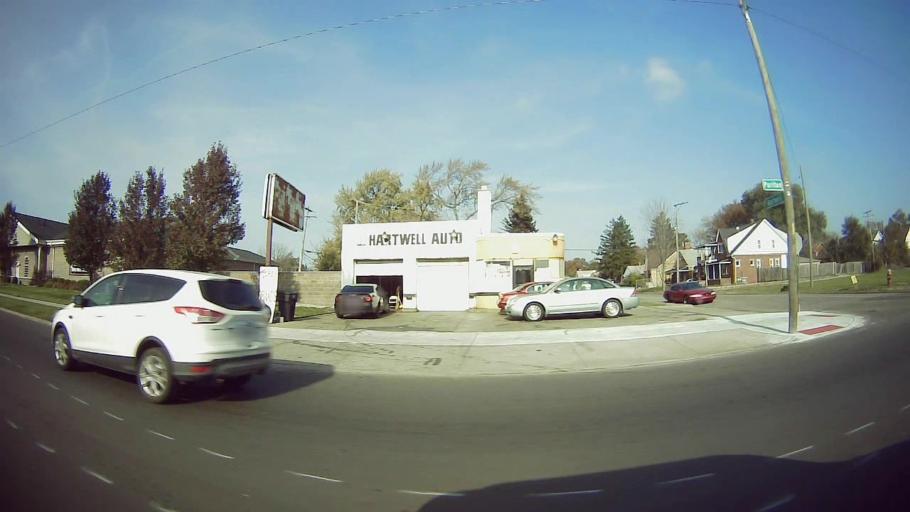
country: US
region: Michigan
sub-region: Oakland County
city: Oak Park
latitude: 42.4094
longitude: -83.1786
